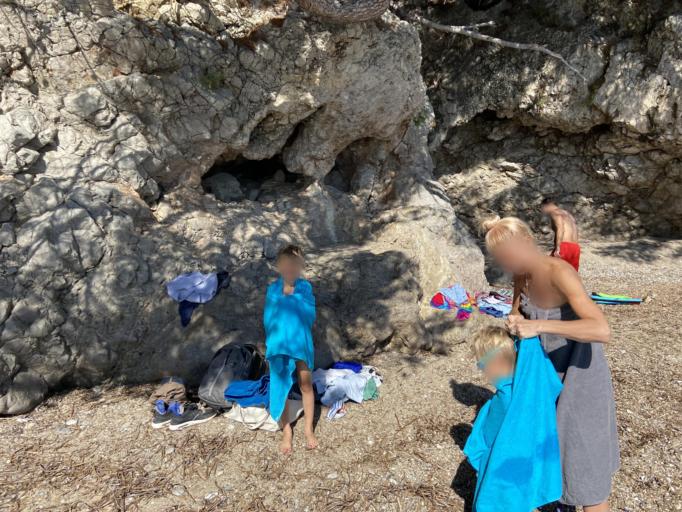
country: FR
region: Provence-Alpes-Cote d'Azur
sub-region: Departement des Alpes-Maritimes
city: Eze
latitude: 43.7221
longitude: 7.3809
